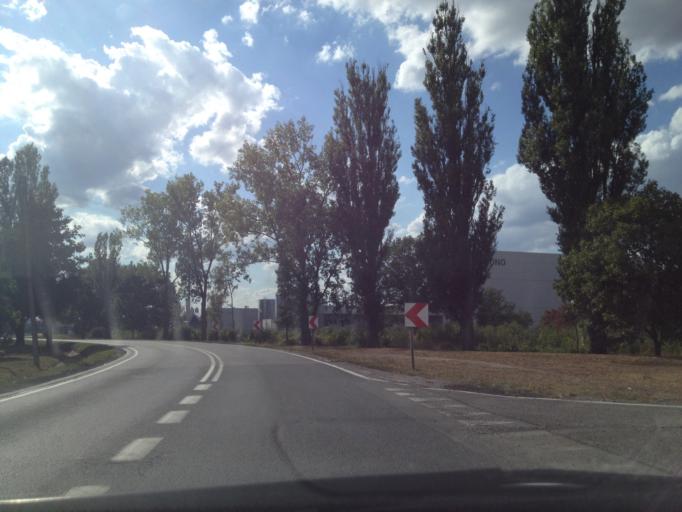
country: PL
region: Lubusz
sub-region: Powiat zarski
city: Zary
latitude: 51.6346
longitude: 15.1132
